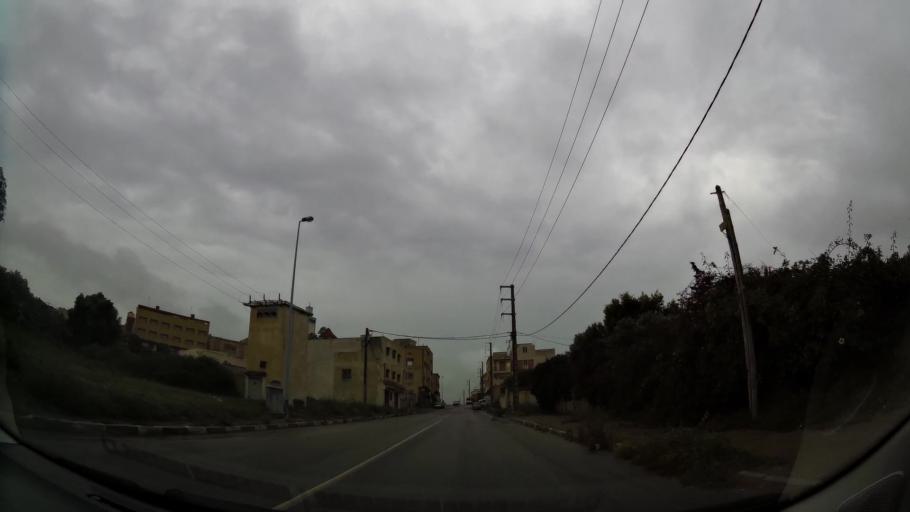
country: MA
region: Oriental
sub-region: Nador
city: Nador
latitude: 35.1527
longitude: -3.0263
